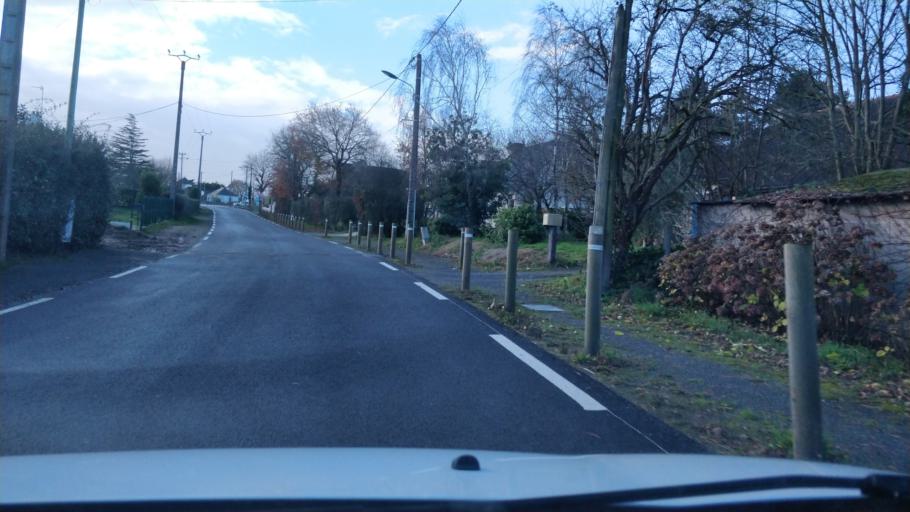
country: FR
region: Pays de la Loire
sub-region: Departement de la Loire-Atlantique
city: Asserac
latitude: 47.4234
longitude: -2.3957
